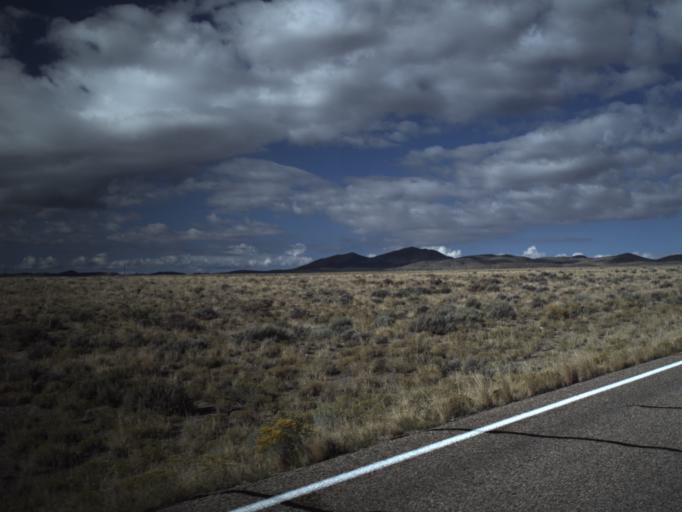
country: US
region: Utah
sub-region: Beaver County
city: Milford
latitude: 38.4423
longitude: -113.1708
